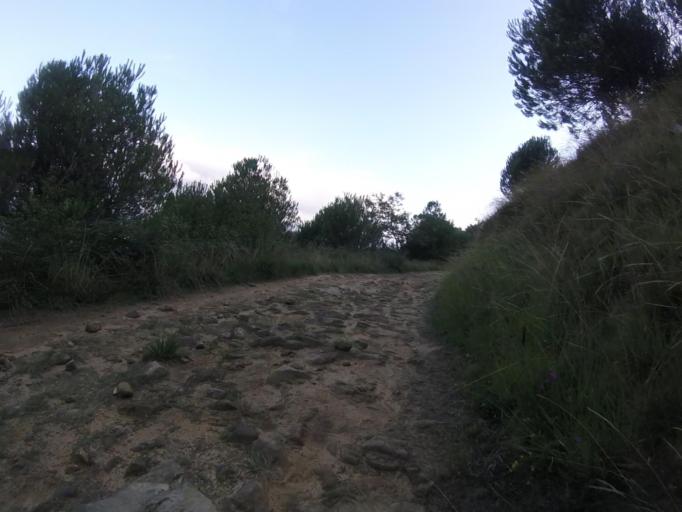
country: ES
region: Basque Country
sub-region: Provincia de Guipuzcoa
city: Fuenterrabia
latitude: 43.3511
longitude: -1.8401
